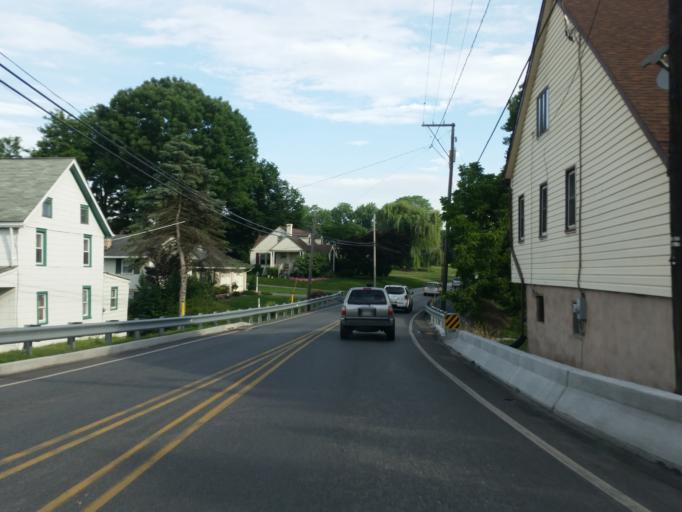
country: US
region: Pennsylvania
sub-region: Lancaster County
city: Lampeter
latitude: 40.0202
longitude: -76.2384
